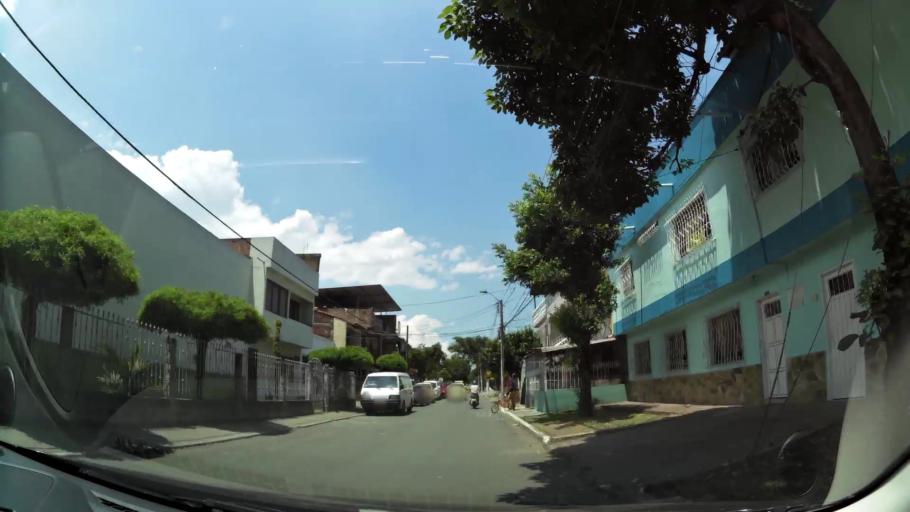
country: CO
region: Valle del Cauca
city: Cali
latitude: 3.4468
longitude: -76.4985
